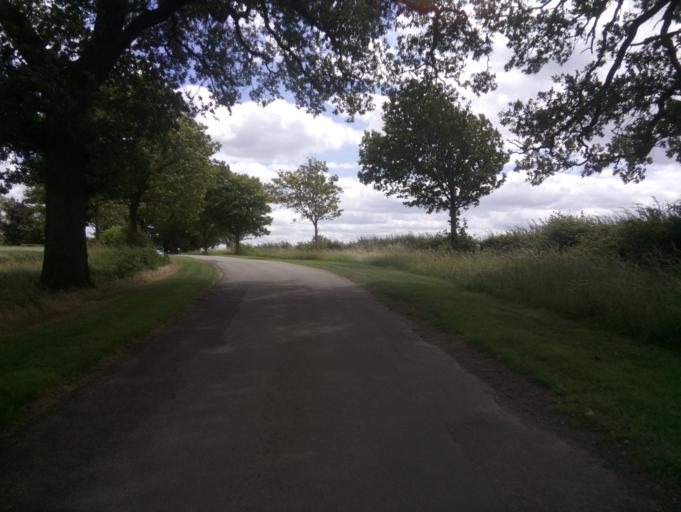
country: GB
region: England
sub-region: Nottinghamshire
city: Cotgrave
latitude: 52.8572
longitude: -1.0508
